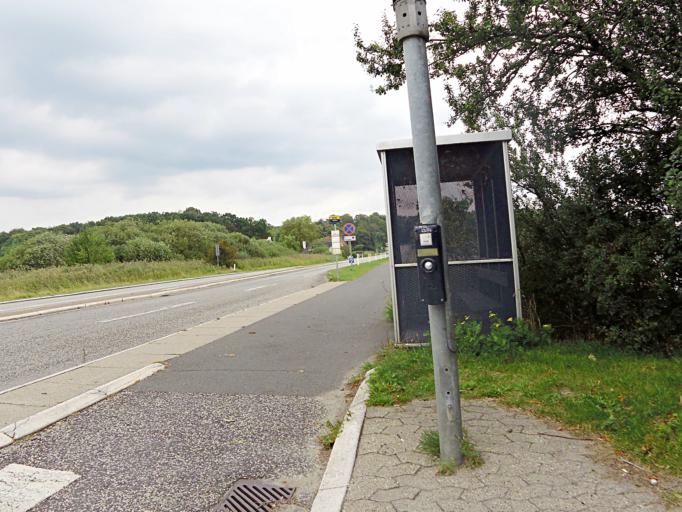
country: DK
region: Capital Region
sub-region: Fredensborg Kommune
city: Niva
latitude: 55.9388
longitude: 12.5237
